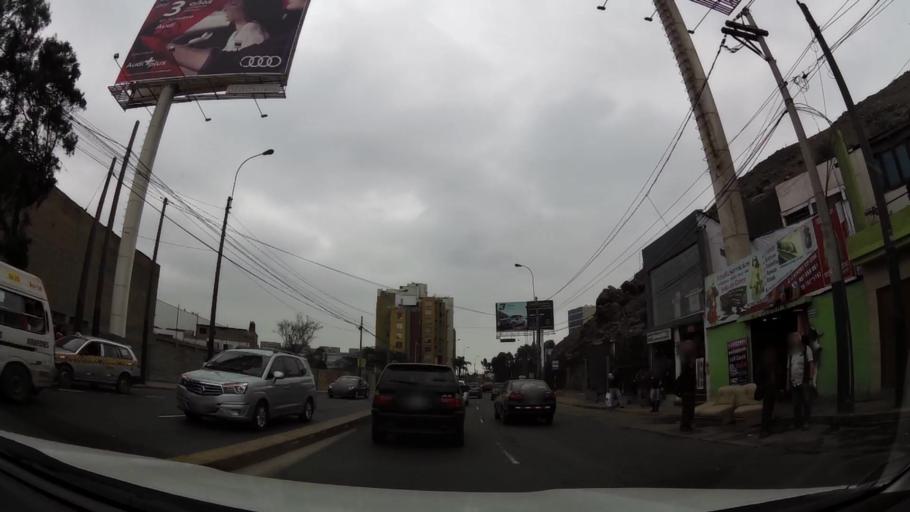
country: PE
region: Lima
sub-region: Lima
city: La Molina
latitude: -12.0953
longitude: -76.9683
